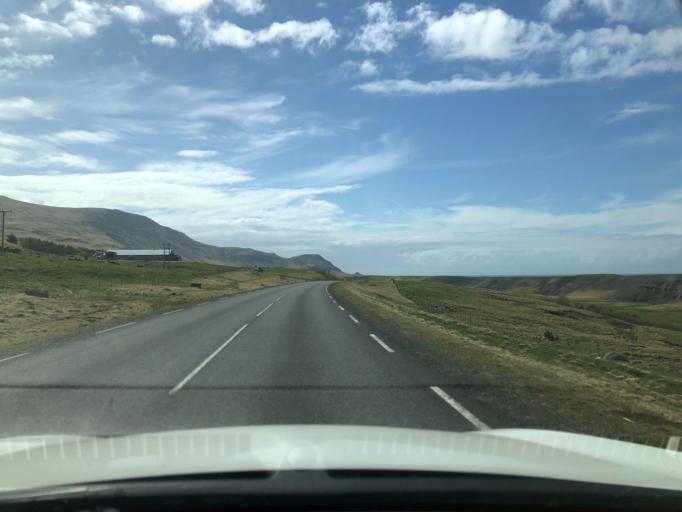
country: IS
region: Capital Region
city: Mosfellsbaer
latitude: 64.3106
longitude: -21.7723
